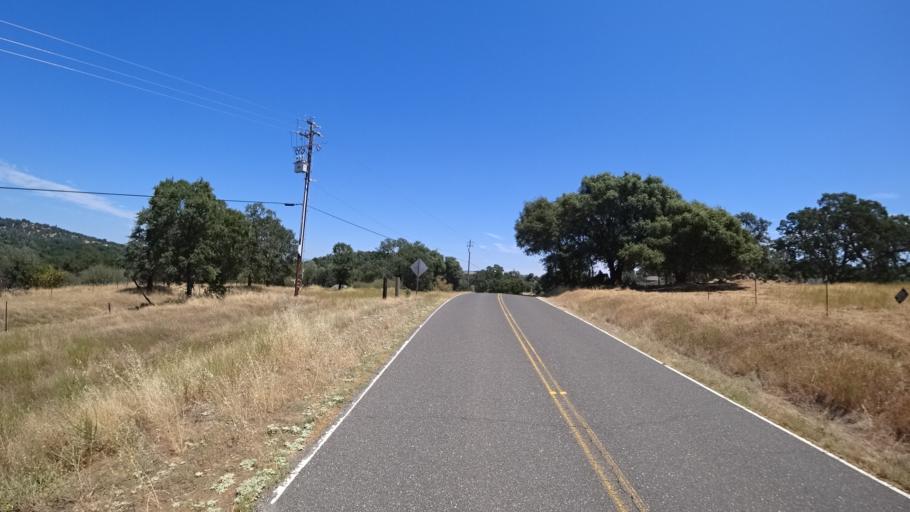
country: US
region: California
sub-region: Calaveras County
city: Angels Camp
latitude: 38.0746
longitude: -120.5688
